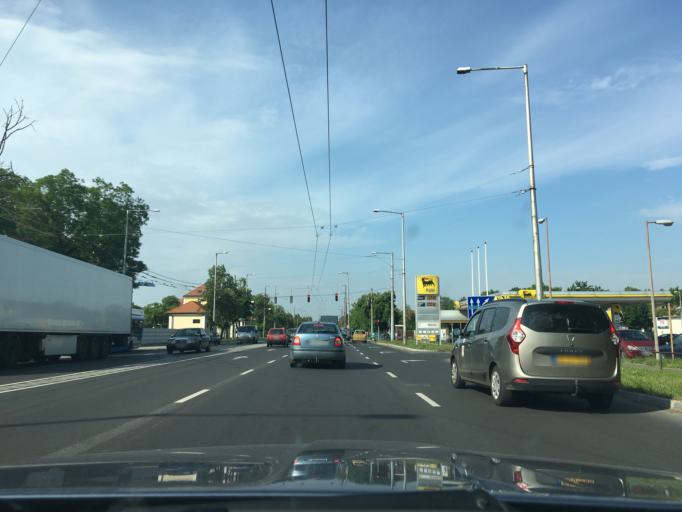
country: HU
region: Hajdu-Bihar
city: Debrecen
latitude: 47.5416
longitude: 21.6410
